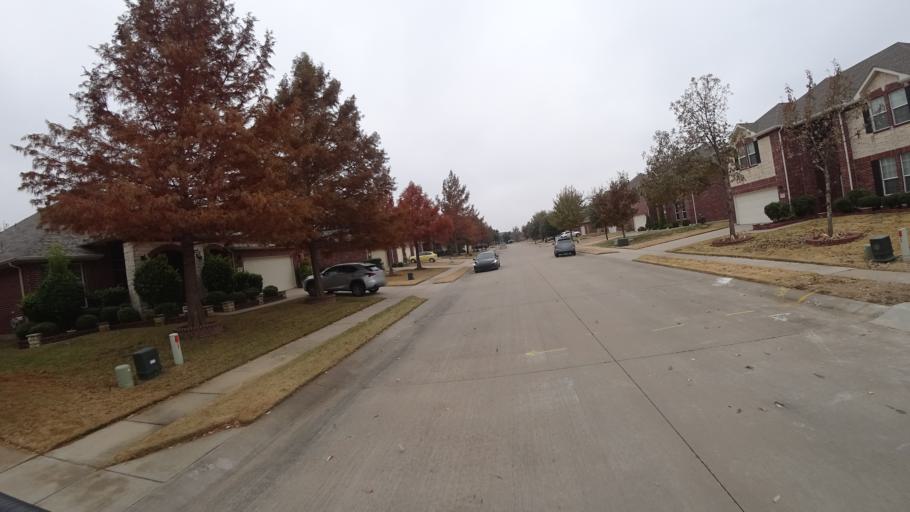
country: US
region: Texas
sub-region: Denton County
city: The Colony
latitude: 33.0670
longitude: -96.9020
